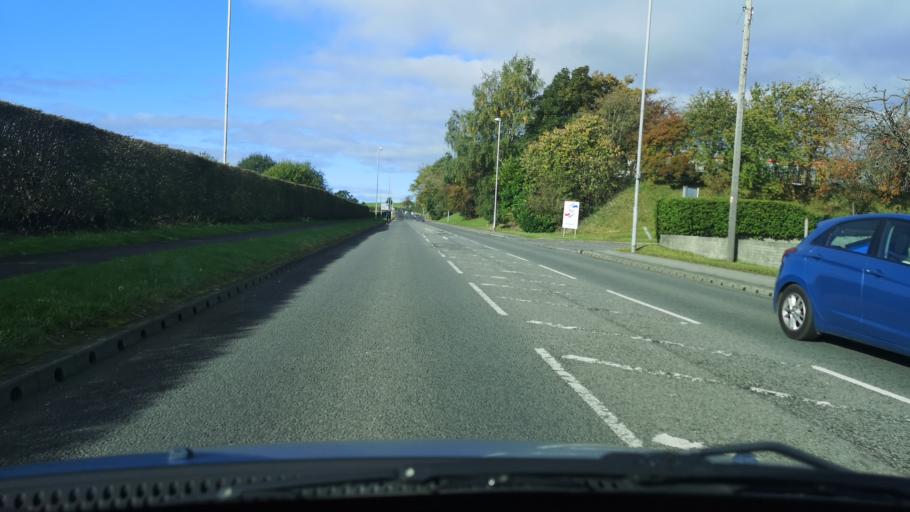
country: GB
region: England
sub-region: City and Borough of Wakefield
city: Featherstone
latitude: 53.6757
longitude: -1.3737
